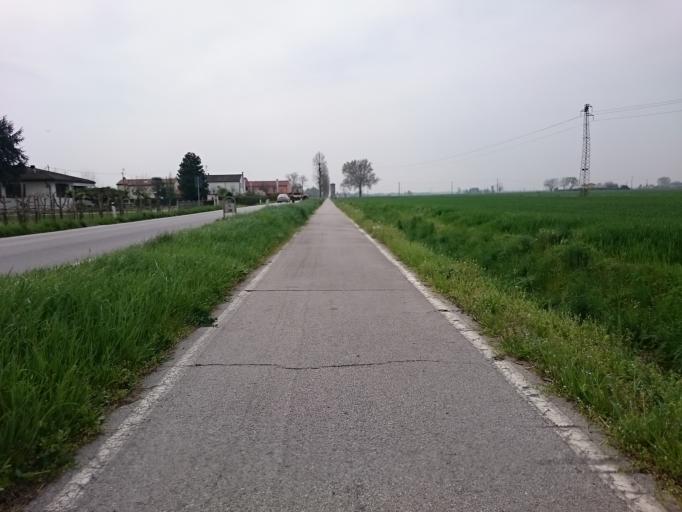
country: IT
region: Veneto
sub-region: Provincia di Padova
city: Bagnoli di Sopra
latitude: 45.1764
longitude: 11.8802
